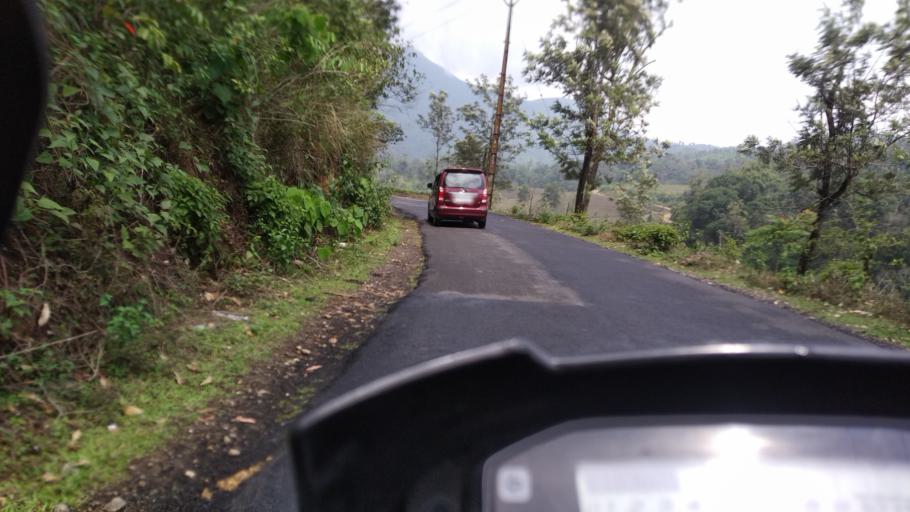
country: IN
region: Kerala
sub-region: Kottayam
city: Erattupetta
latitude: 9.6329
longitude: 76.9607
